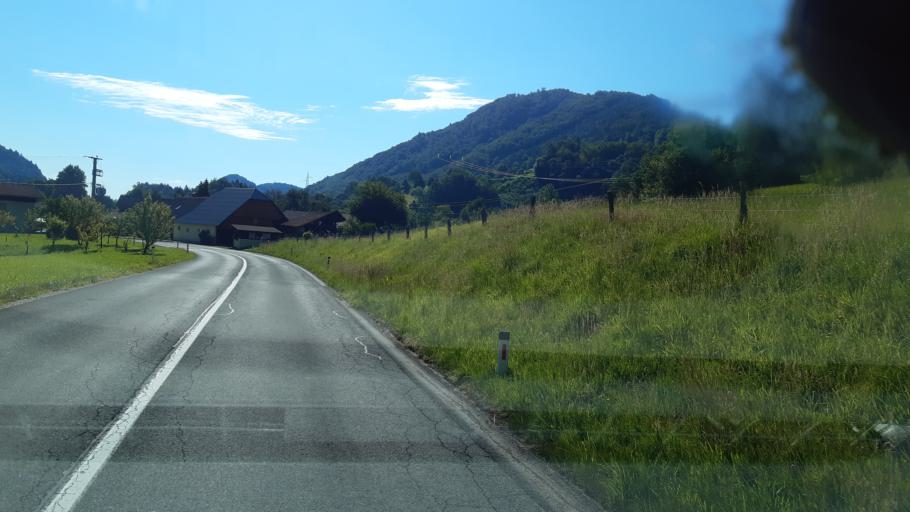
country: SI
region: Gornji Grad
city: Gornji Grad
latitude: 46.2149
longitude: 14.8307
